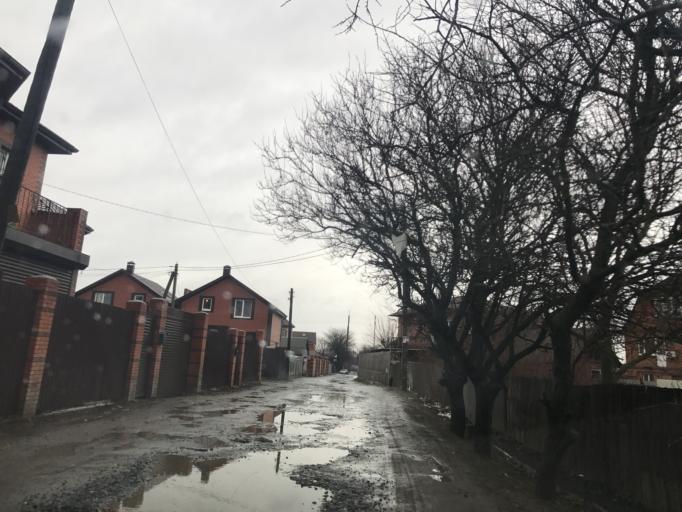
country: RU
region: Rostov
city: Severnyy
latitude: 47.2437
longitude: 39.6222
